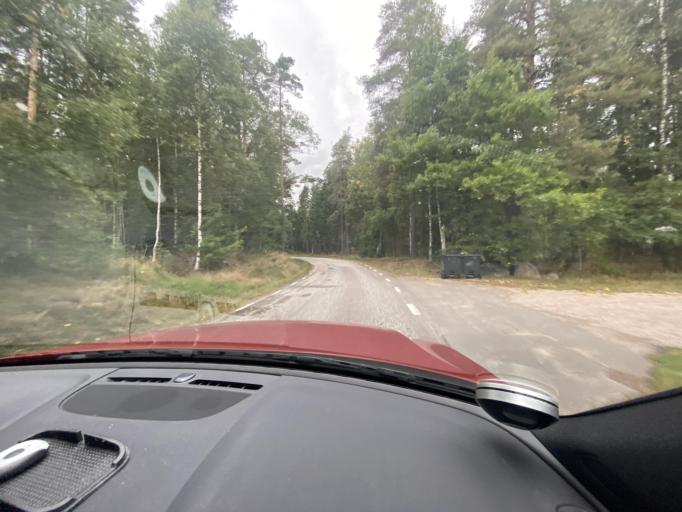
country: SE
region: Kronoberg
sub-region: Markaryds Kommun
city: Markaryd
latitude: 56.4966
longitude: 13.5713
